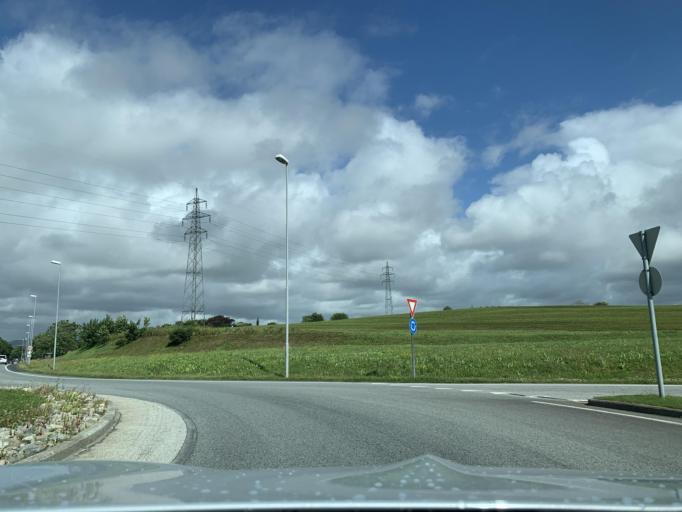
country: NO
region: Rogaland
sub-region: Klepp
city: Kleppe
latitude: 58.7842
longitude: 5.6383
